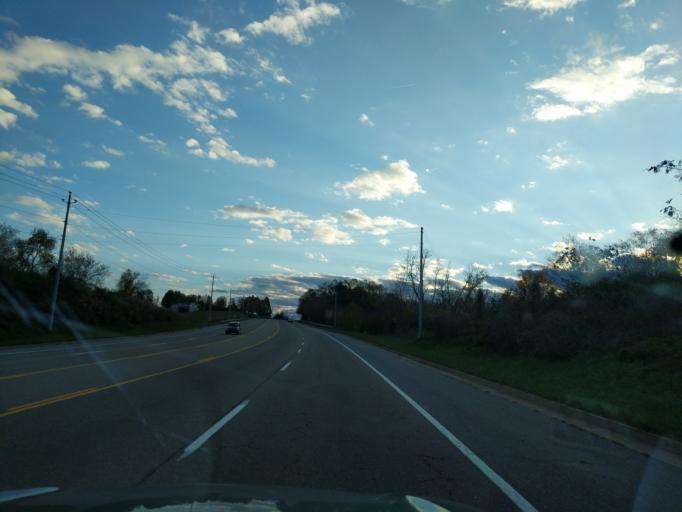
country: US
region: Tennessee
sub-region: Washington County
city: Spurgeon
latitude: 36.4309
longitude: -82.4550
